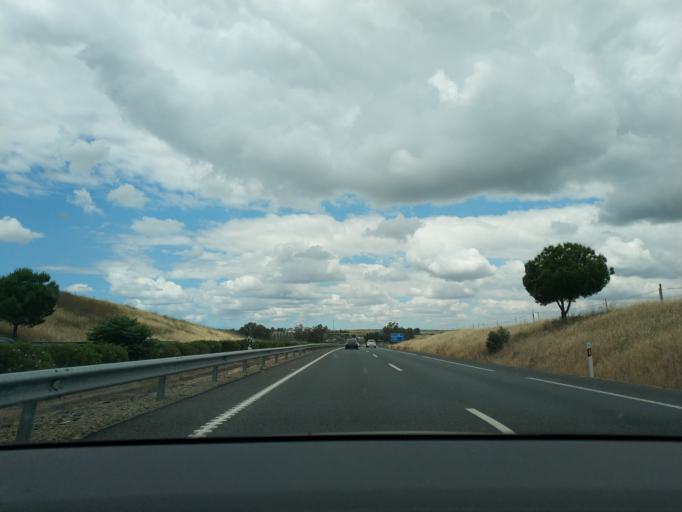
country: ES
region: Andalusia
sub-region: Provincia de Sevilla
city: Sanlucar la Mayor
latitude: 37.3643
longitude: -6.2592
